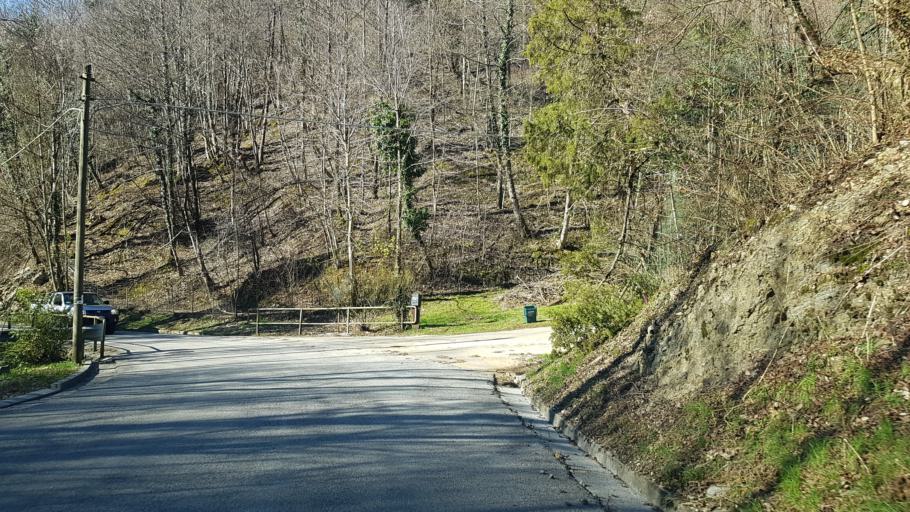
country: IT
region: Friuli Venezia Giulia
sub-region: Provincia di Udine
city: Nimis
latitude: 46.2242
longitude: 13.2985
